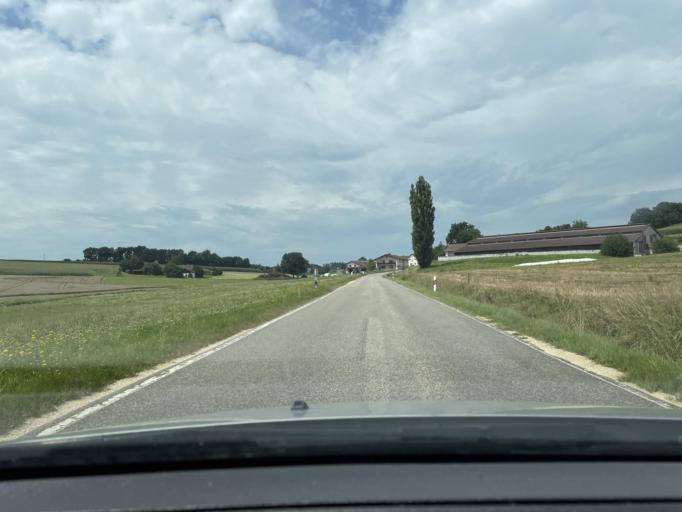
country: DE
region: Bavaria
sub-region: Lower Bavaria
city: Geisenhausen
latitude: 48.4379
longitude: 12.2782
